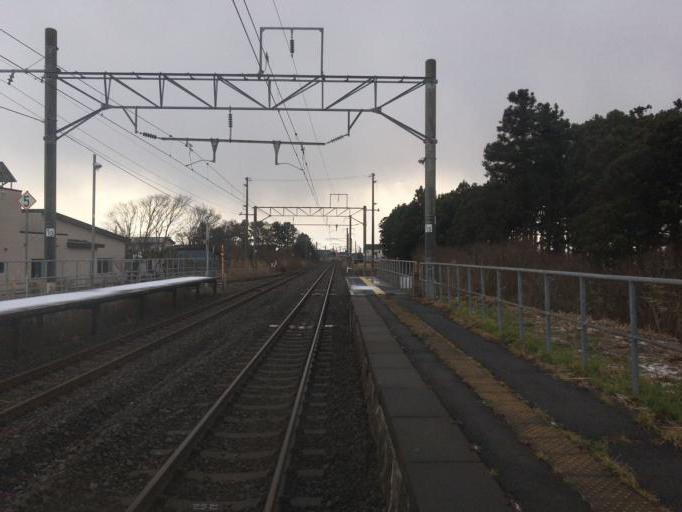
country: JP
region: Aomori
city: Aomori Shi
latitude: 40.9026
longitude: 140.6723
